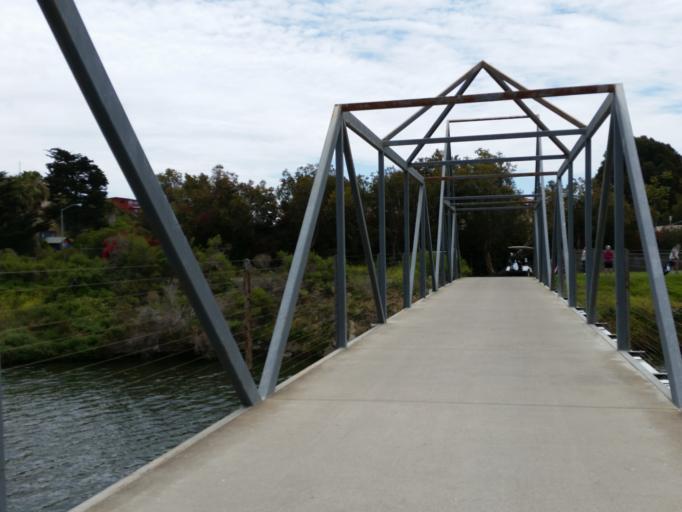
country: US
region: California
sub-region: San Luis Obispo County
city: Avila Beach
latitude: 35.1829
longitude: -120.7327
